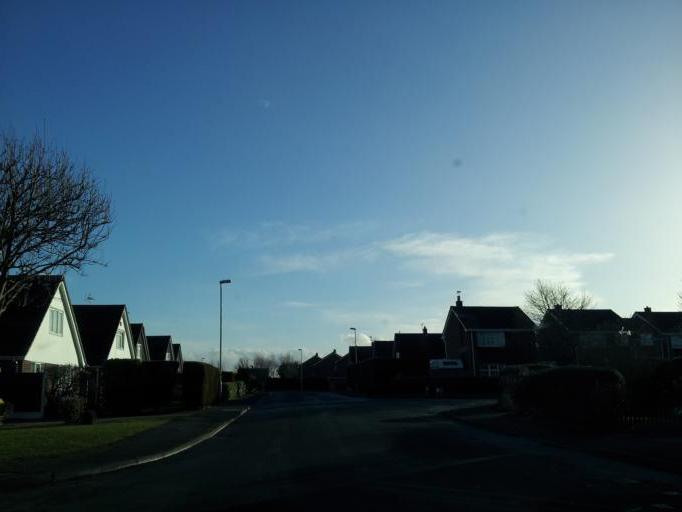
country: GB
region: England
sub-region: Nottinghamshire
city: Newark on Trent
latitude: 53.0759
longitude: -0.7795
